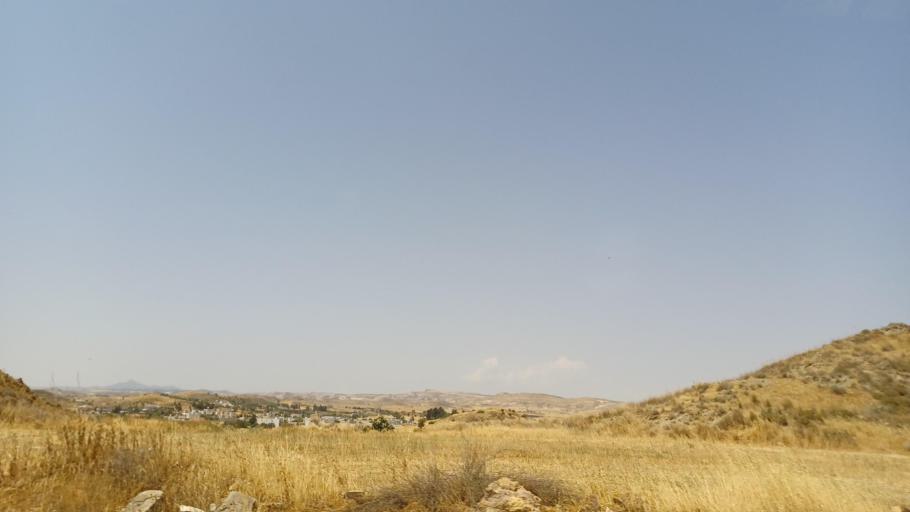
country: CY
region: Larnaka
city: Troulloi
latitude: 35.0325
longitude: 33.6229
